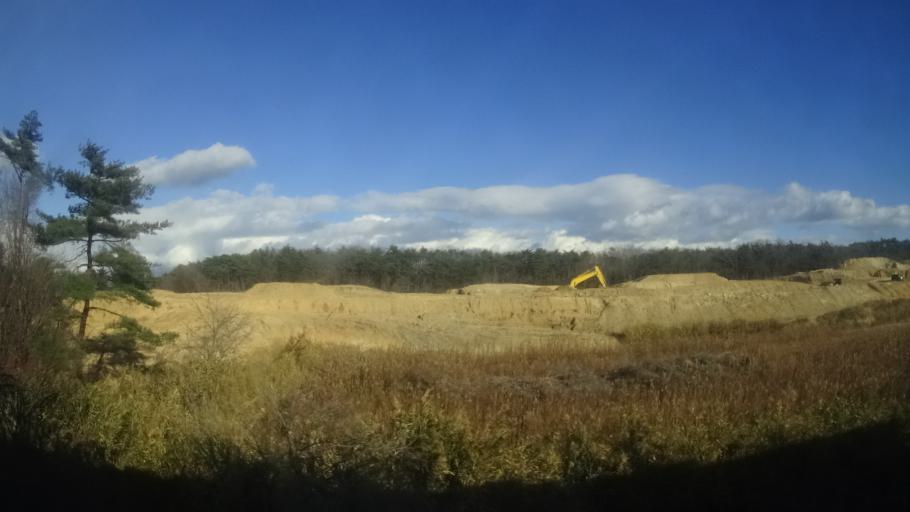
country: JP
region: Miyagi
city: Marumori
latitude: 37.7464
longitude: 140.9414
